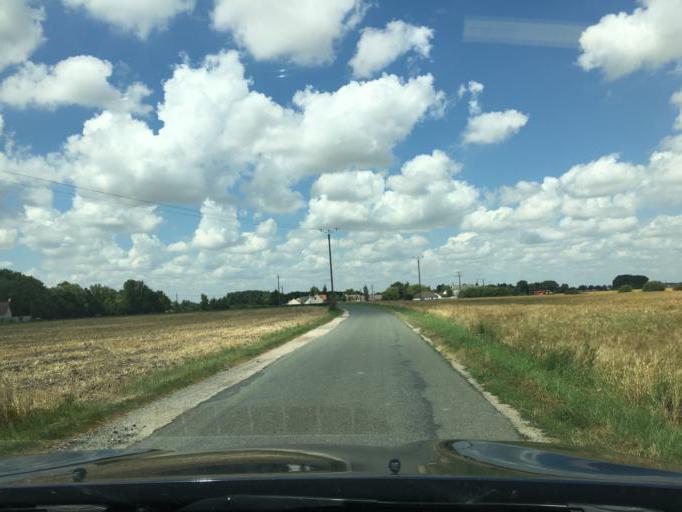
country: FR
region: Centre
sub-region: Departement du Loiret
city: Chevilly
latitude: 48.0263
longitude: 1.9205
